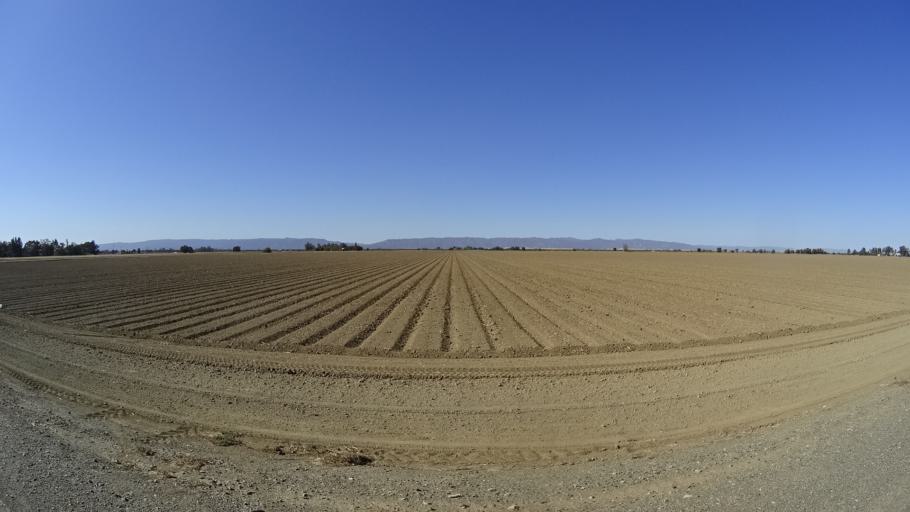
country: US
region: California
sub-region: Solano County
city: Dixon
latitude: 38.5511
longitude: -121.8584
